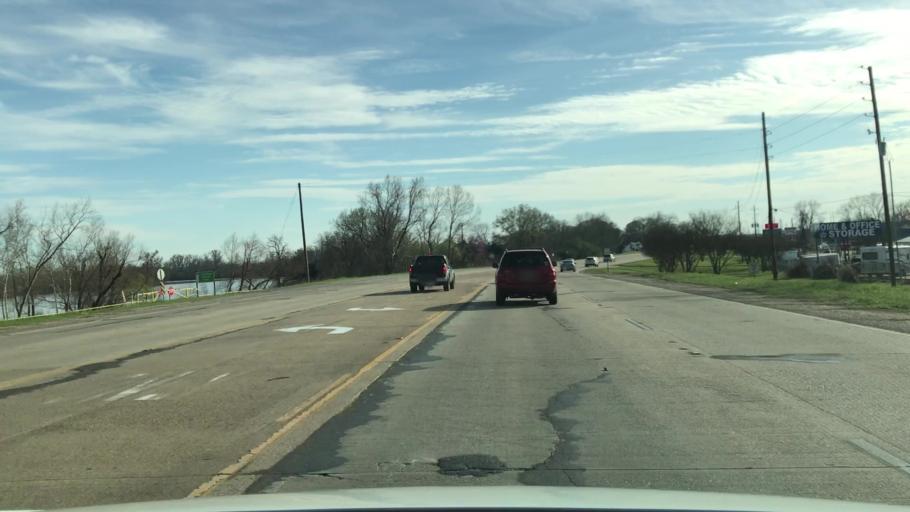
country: US
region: Louisiana
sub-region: Bossier Parish
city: Bossier City
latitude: 32.4450
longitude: -93.7023
